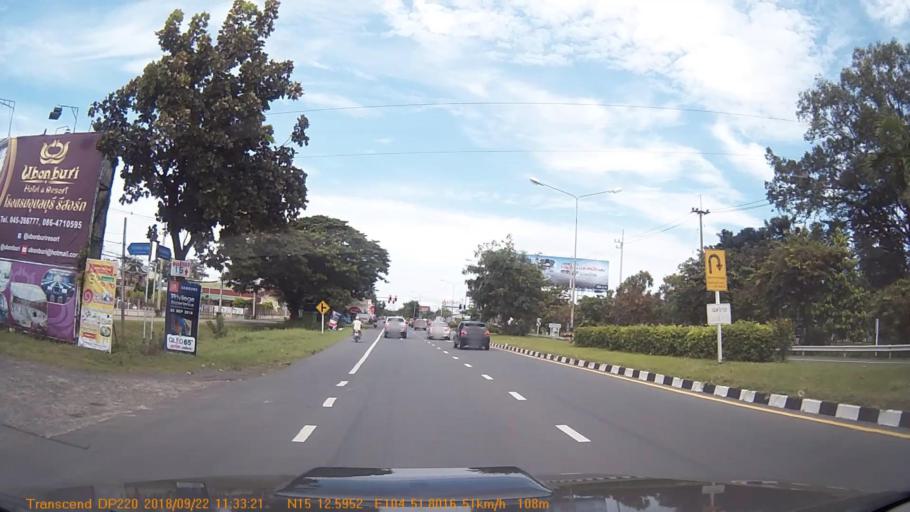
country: TH
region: Changwat Ubon Ratchathani
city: Warin Chamrap
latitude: 15.2099
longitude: 104.8634
